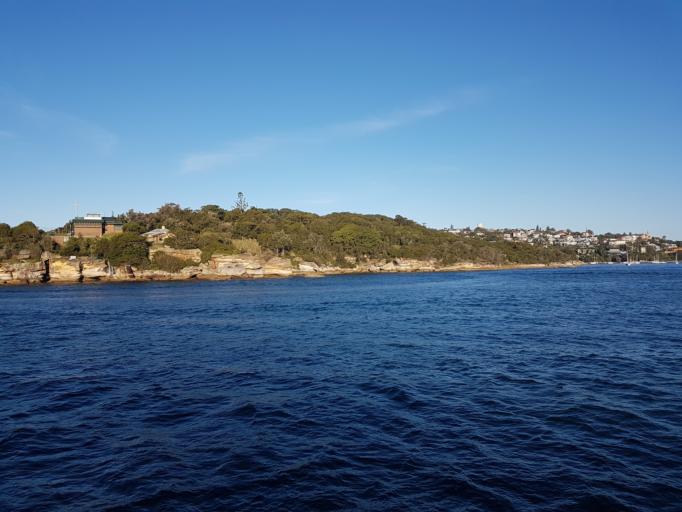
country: AU
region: New South Wales
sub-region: Woollahra
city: Point Piper
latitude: -33.8511
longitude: 151.2621
